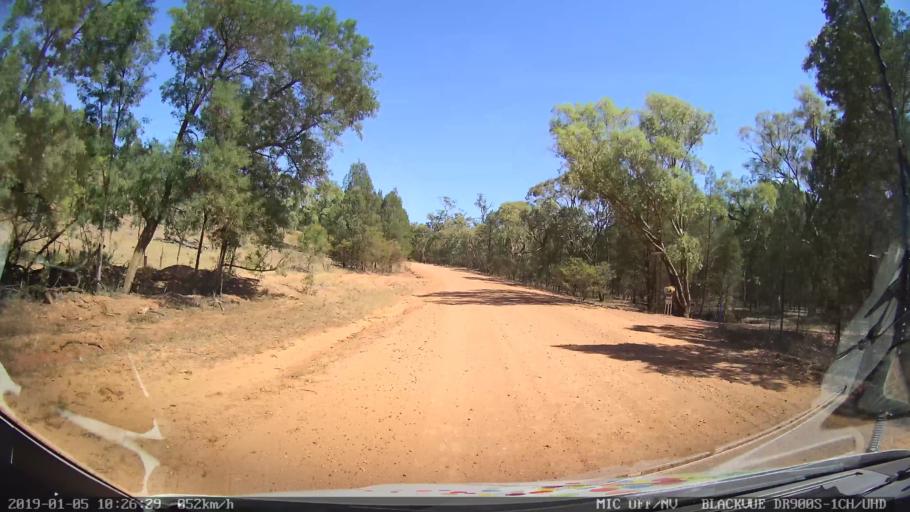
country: AU
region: New South Wales
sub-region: Gilgandra
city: Gilgandra
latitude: -31.5534
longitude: 148.9548
